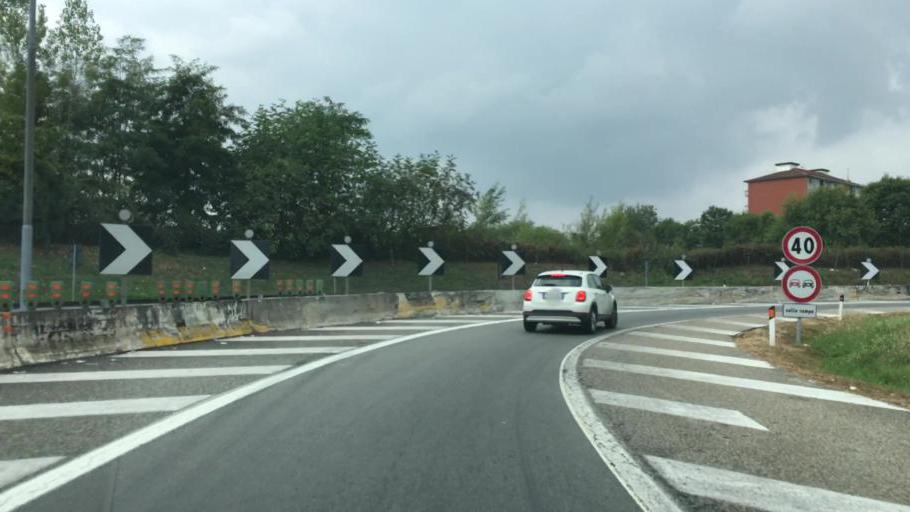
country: IT
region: Piedmont
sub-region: Provincia di Torino
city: Turin
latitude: 45.1033
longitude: 7.6901
